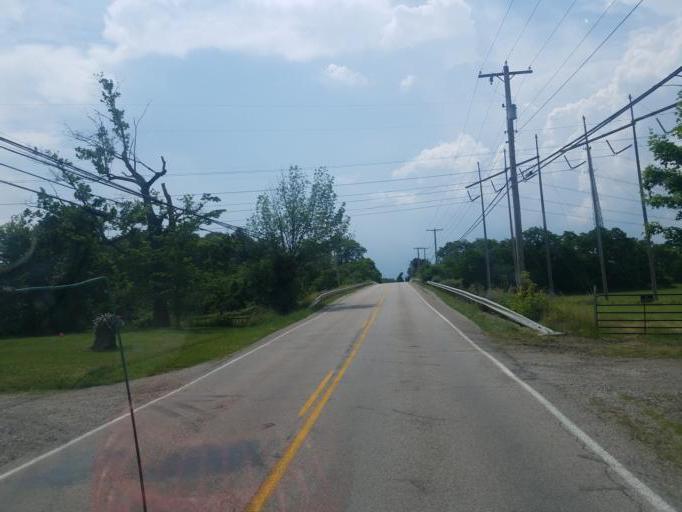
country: US
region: Ohio
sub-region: Portage County
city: Ravenna
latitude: 41.0984
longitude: -81.2012
